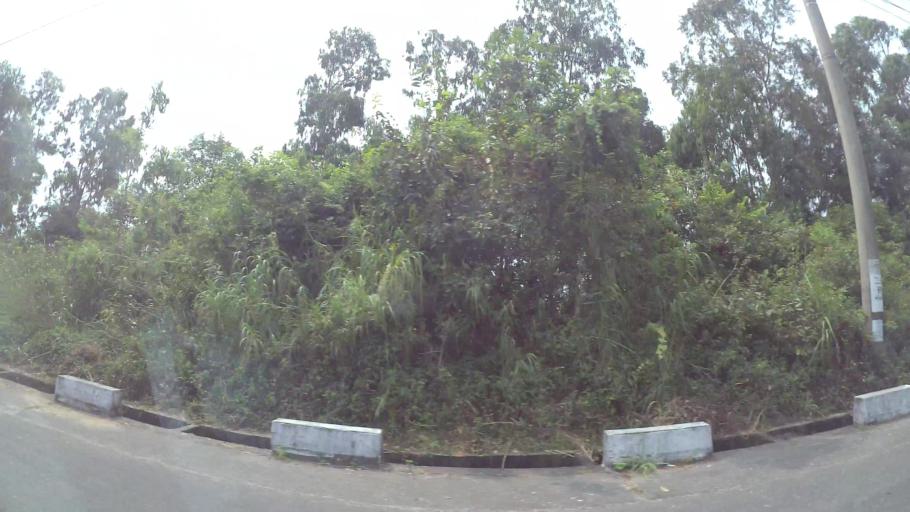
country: VN
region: Da Nang
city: Son Tra
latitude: 16.0993
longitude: 108.2694
